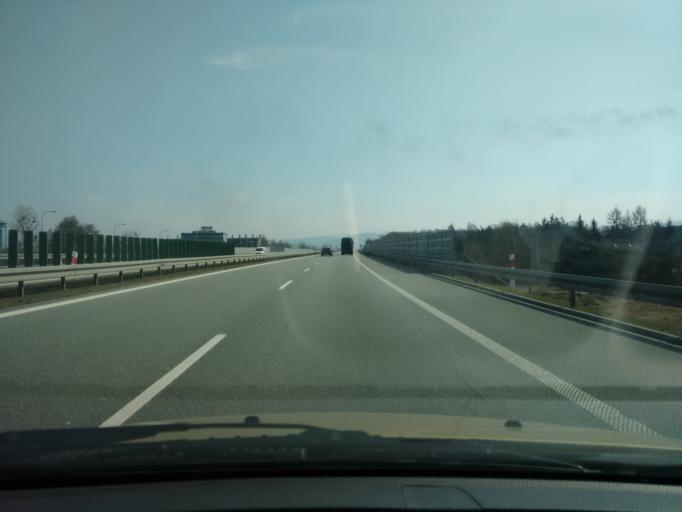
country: PL
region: Silesian Voivodeship
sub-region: Powiat cieszynski
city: Skoczow
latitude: 49.7890
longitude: 18.7687
